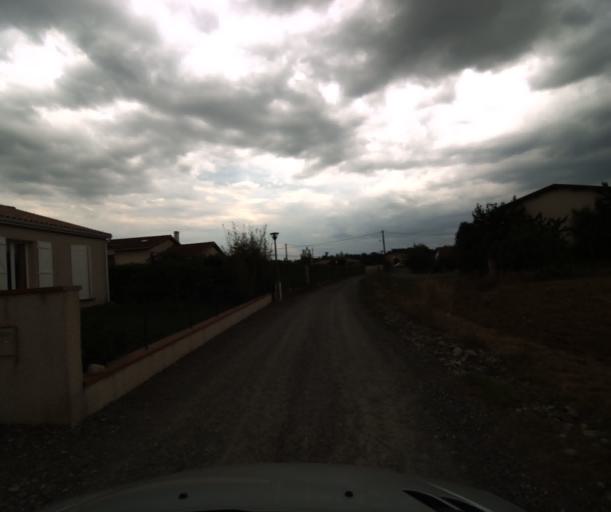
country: FR
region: Midi-Pyrenees
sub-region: Departement de la Haute-Garonne
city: Labastidette
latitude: 43.4631
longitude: 1.2120
